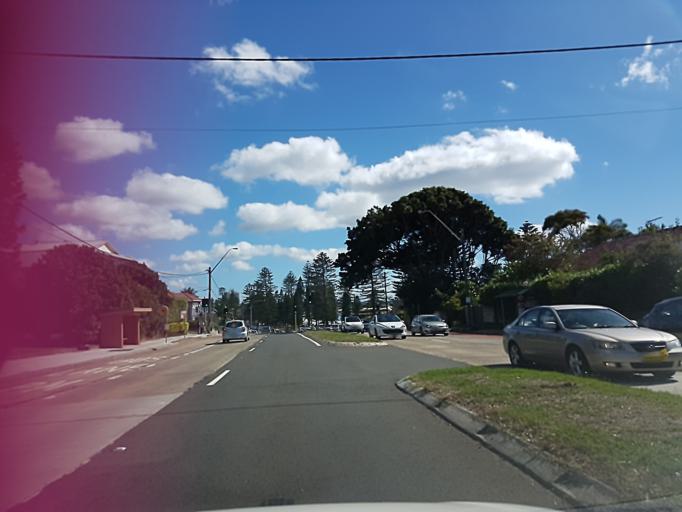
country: AU
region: New South Wales
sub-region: Warringah
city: Dee Why
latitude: -33.7352
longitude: 151.3023
